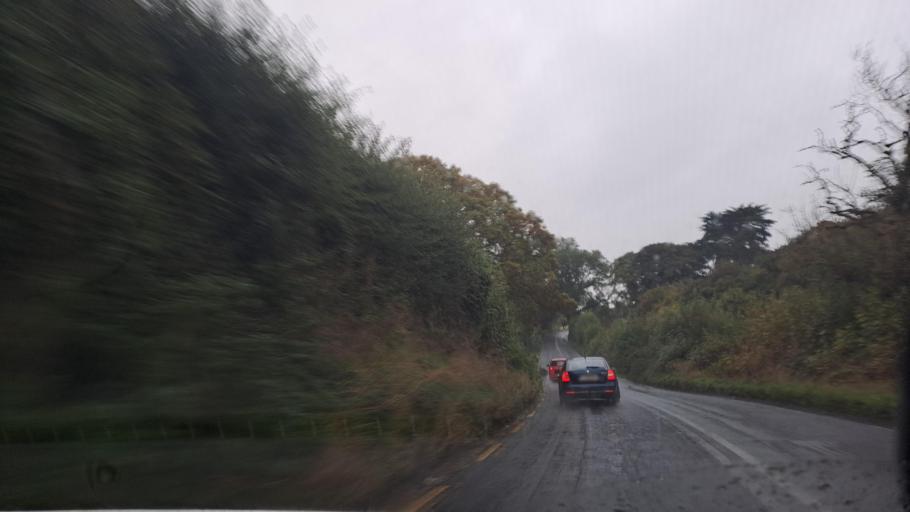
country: IE
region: Leinster
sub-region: Lu
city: Dundalk
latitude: 53.9920
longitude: -6.4631
